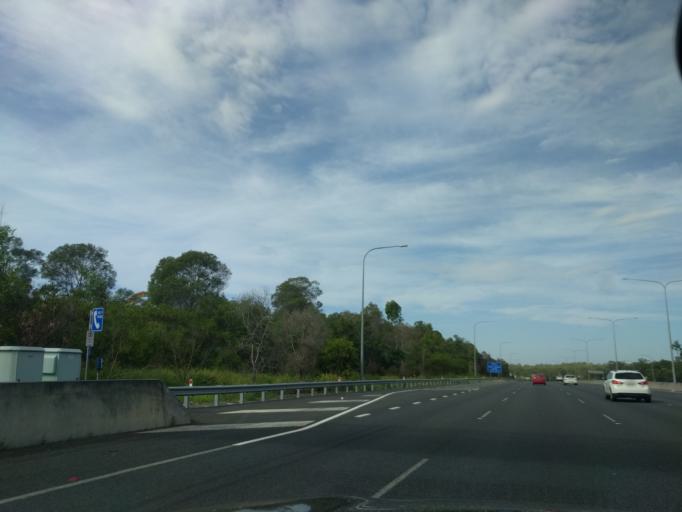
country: AU
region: Queensland
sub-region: Brisbane
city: Wacol
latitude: -27.5820
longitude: 152.9345
